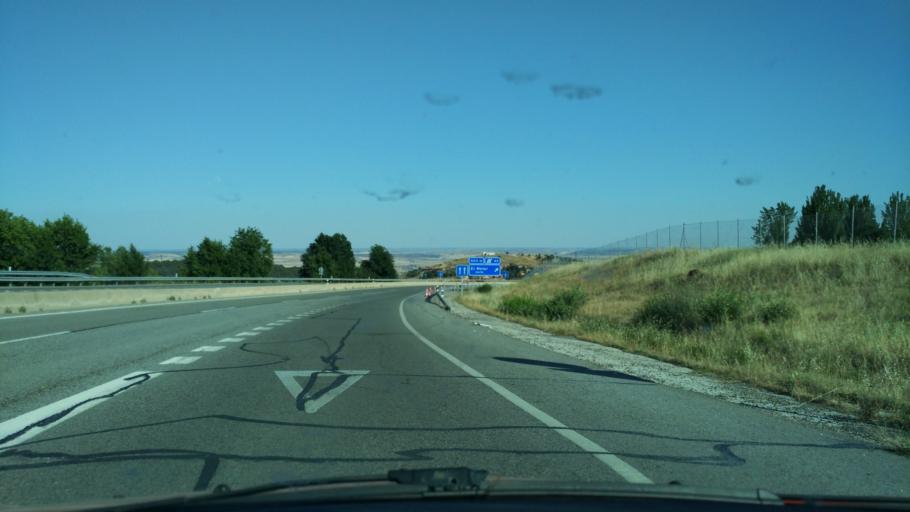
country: ES
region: Madrid
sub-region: Provincia de Madrid
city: Pedrezuela
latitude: 40.7435
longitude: -3.5902
